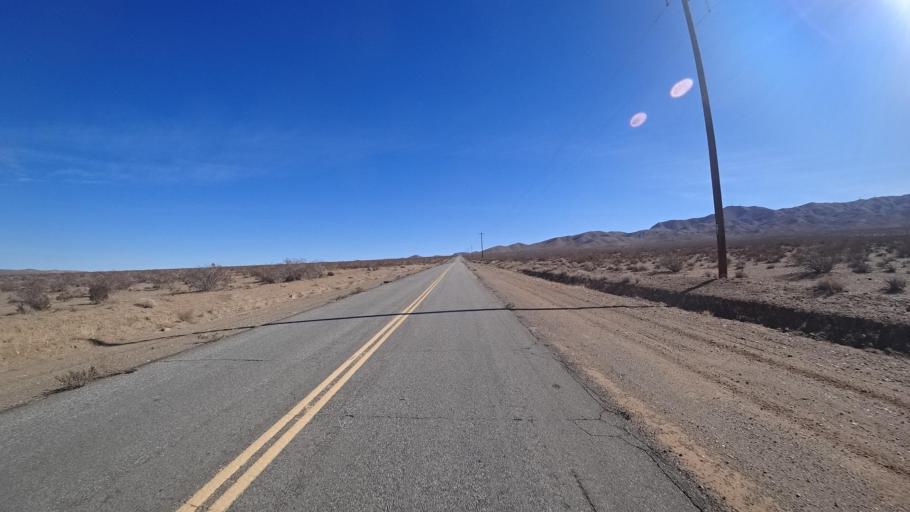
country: US
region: California
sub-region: Kern County
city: Ridgecrest
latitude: 35.3836
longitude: -117.7091
